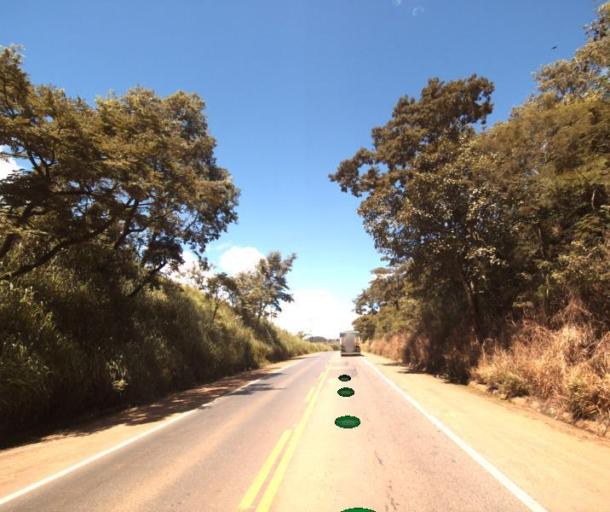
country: BR
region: Goias
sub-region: Anapolis
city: Anapolis
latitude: -16.1675
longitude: -49.0433
